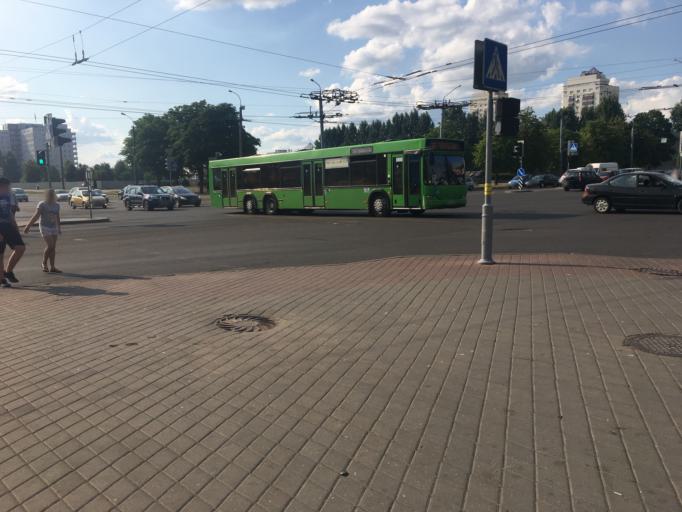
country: BY
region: Grodnenskaya
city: Hrodna
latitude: 53.6716
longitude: 23.8037
